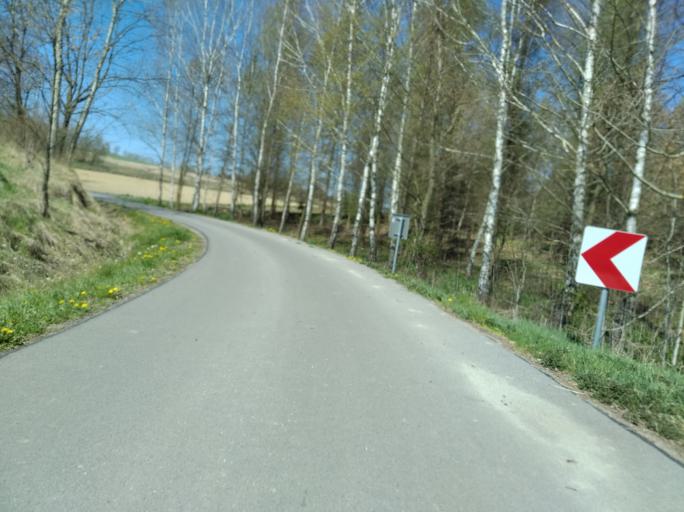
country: PL
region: Subcarpathian Voivodeship
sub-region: Powiat strzyzowski
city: Wisniowa
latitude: 49.9047
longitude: 21.6817
